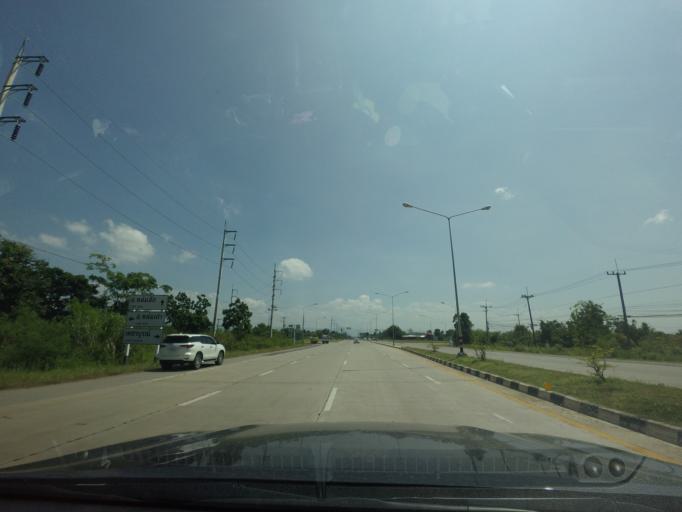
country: TH
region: Phetchabun
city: Lom Sak
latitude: 16.7660
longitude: 101.1842
